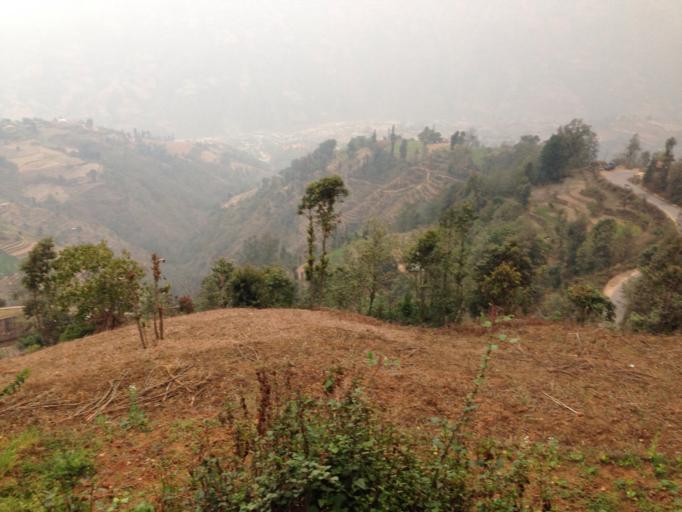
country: NP
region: Central Region
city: Kirtipur
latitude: 27.7264
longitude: 85.1065
